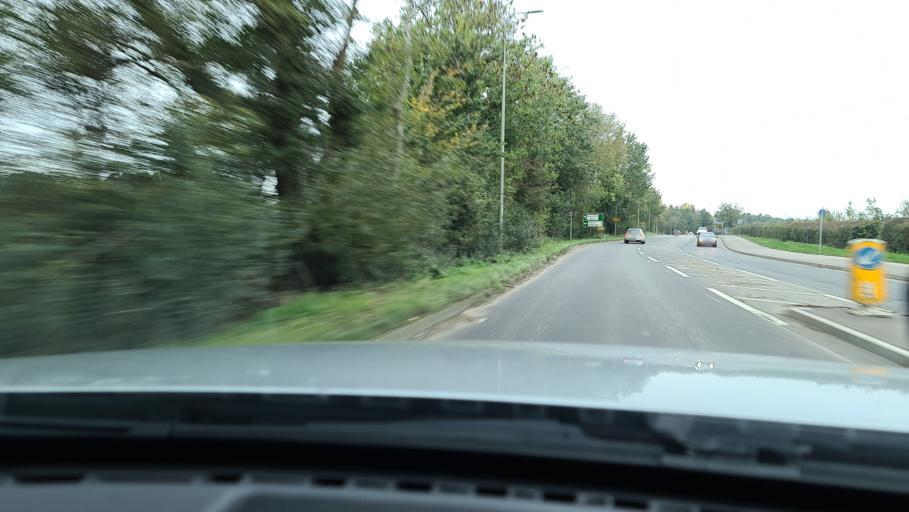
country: GB
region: England
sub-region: Oxfordshire
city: Bicester
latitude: 51.8798
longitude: -1.1259
